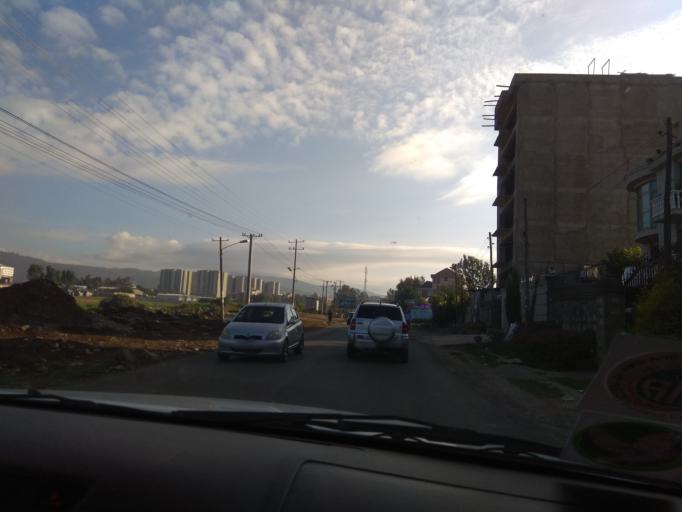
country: ET
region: Adis Abeba
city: Addis Ababa
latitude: 8.9933
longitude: 38.8034
